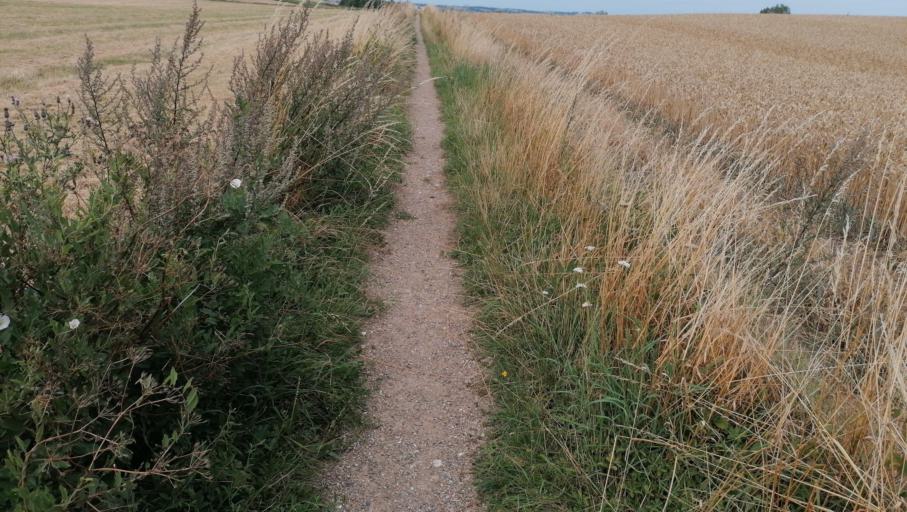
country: DK
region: Zealand
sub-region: Odsherred Kommune
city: Horve
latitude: 55.7494
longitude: 11.4293
